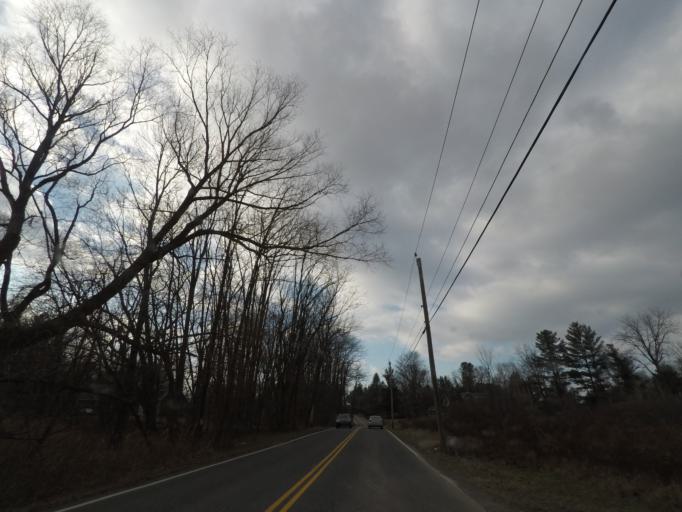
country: US
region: New York
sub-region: Albany County
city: McKownville
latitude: 42.6663
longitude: -73.8572
